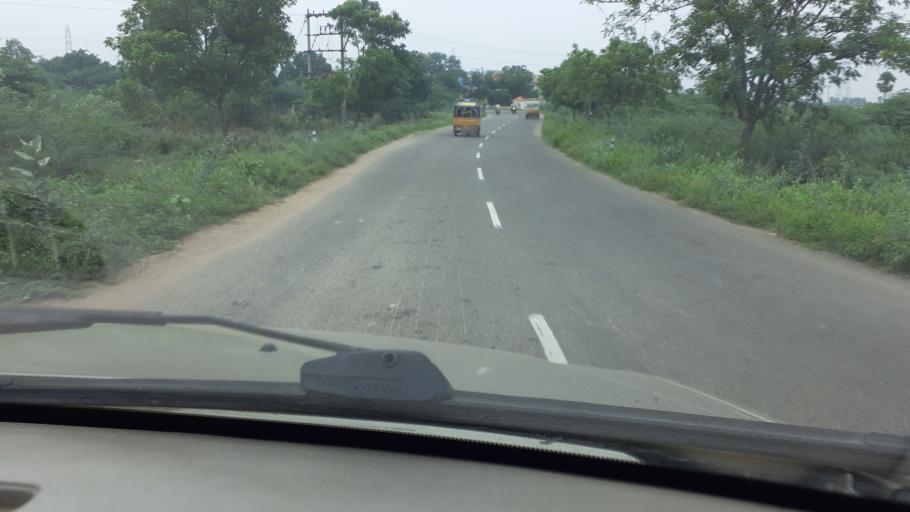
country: IN
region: Tamil Nadu
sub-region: Tirunelveli Kattabo
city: Nanguneri
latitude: 8.4925
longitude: 77.6481
